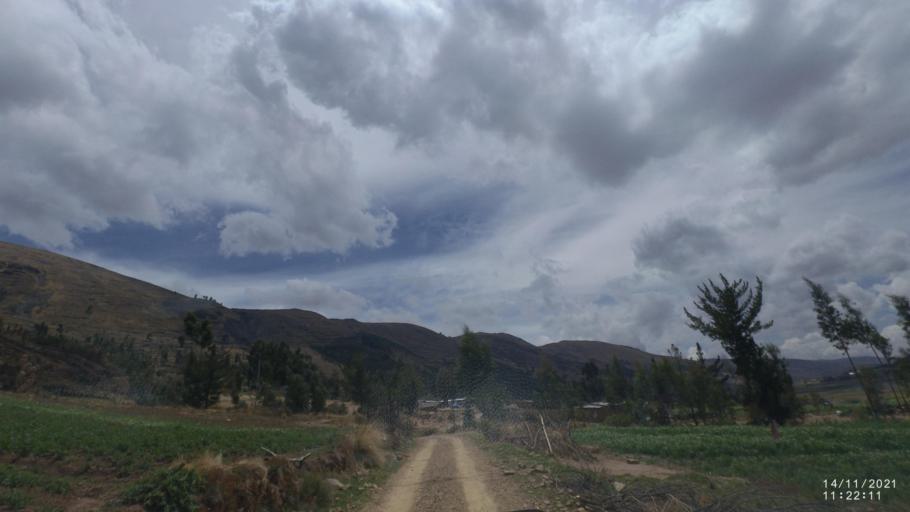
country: BO
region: Cochabamba
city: Cochabamba
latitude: -17.3358
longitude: -66.0336
